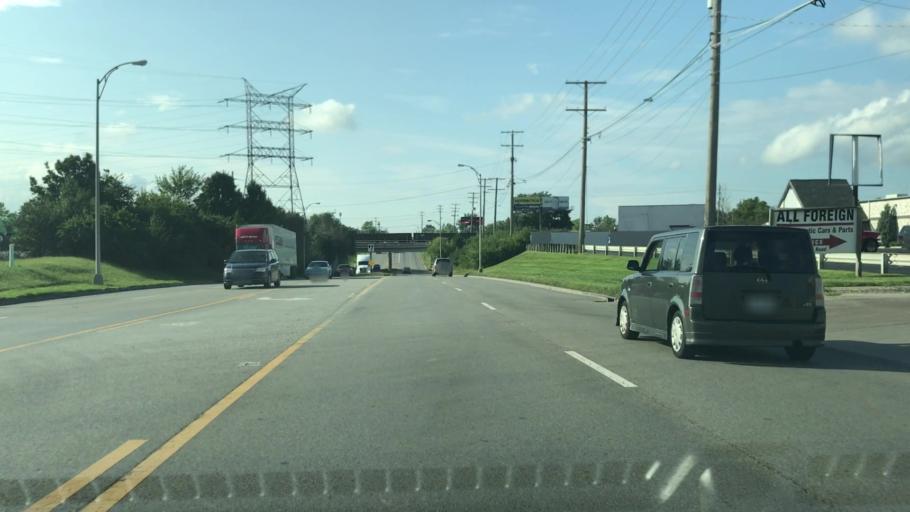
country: US
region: Ohio
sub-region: Franklin County
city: Lincoln Village
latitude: 39.9636
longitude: -83.0932
